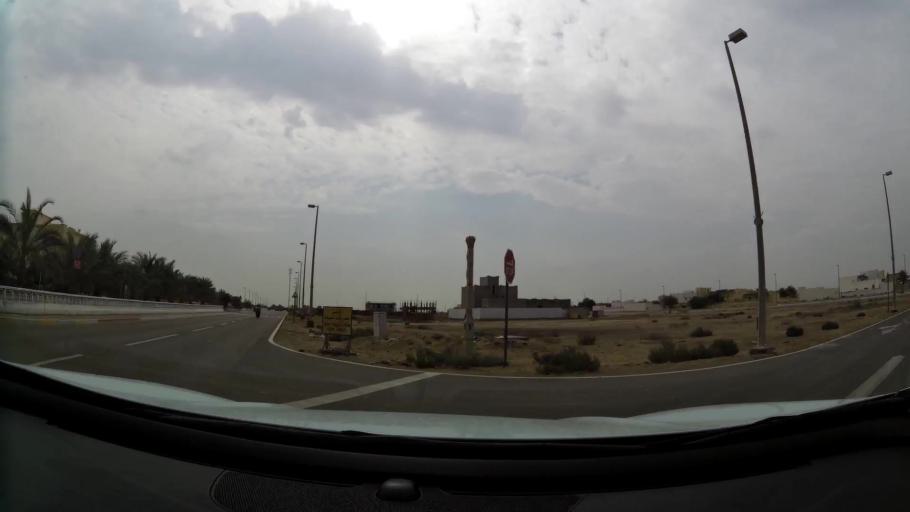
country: AE
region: Abu Dhabi
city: Abu Dhabi
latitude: 24.6327
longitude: 54.7165
